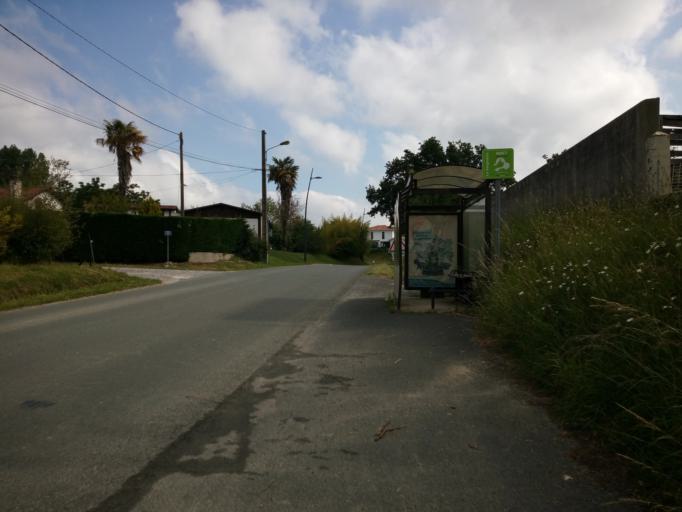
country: FR
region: Aquitaine
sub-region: Departement des Landes
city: Saint-Andre-de-Seignanx
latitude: 43.5672
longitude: -1.3612
